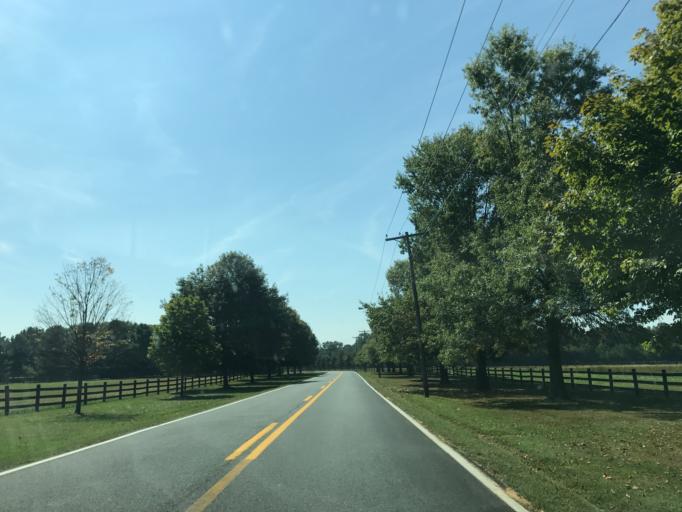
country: US
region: Delaware
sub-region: New Castle County
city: Middletown
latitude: 39.5033
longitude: -75.8028
